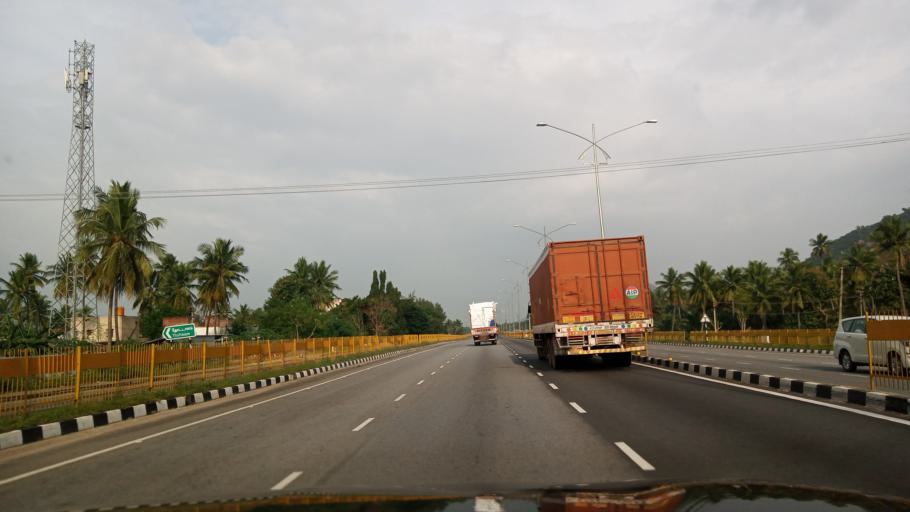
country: IN
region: Tamil Nadu
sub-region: Vellore
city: Gudiyatham
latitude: 12.8612
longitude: 78.8319
